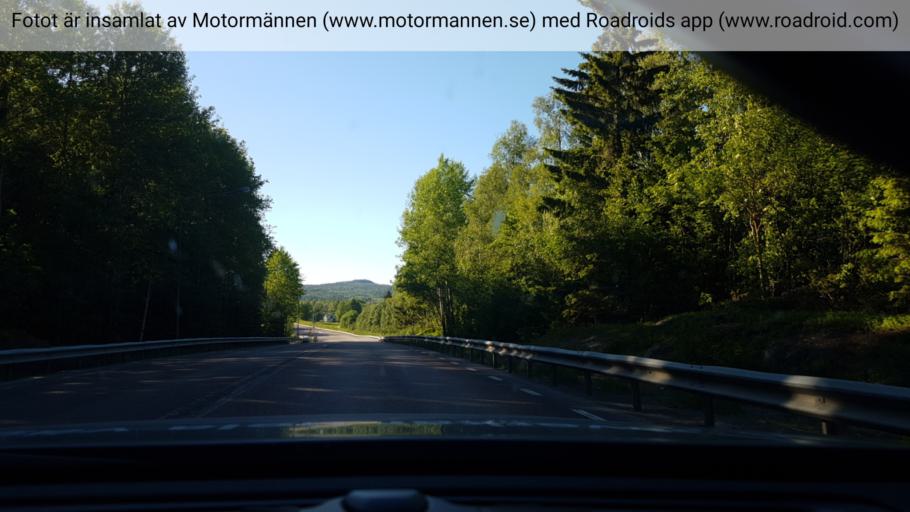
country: SE
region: Vaesternorrland
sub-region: Haernoesands Kommun
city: Haernoesand
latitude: 62.6614
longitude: 17.8578
